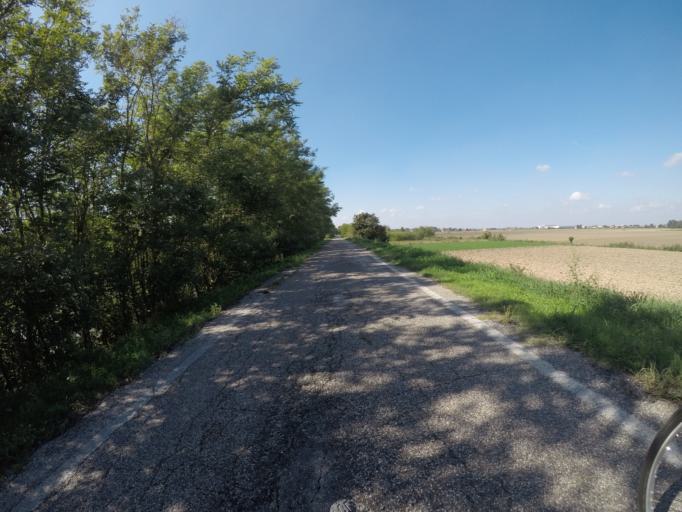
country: IT
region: Veneto
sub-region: Provincia di Rovigo
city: Frassinelle Polesine
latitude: 44.9984
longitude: 11.6954
